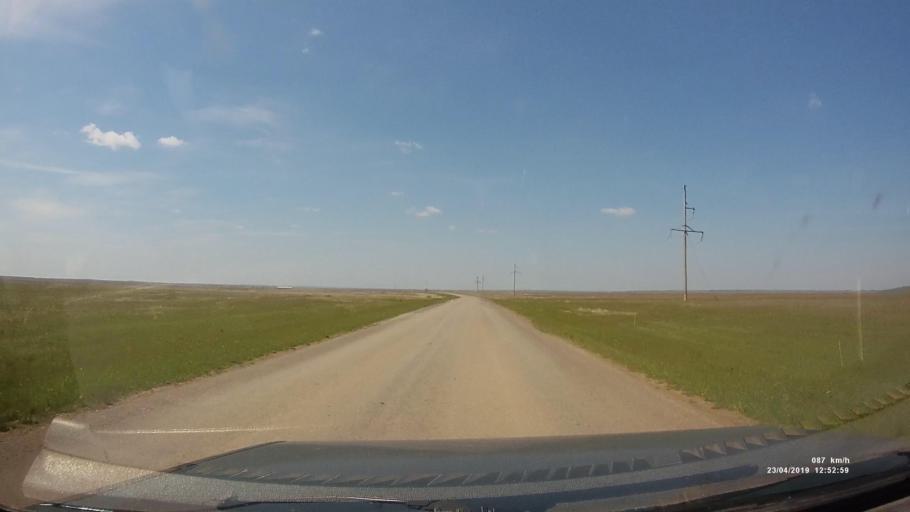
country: RU
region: Kalmykiya
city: Yashalta
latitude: 46.5700
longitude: 42.6020
